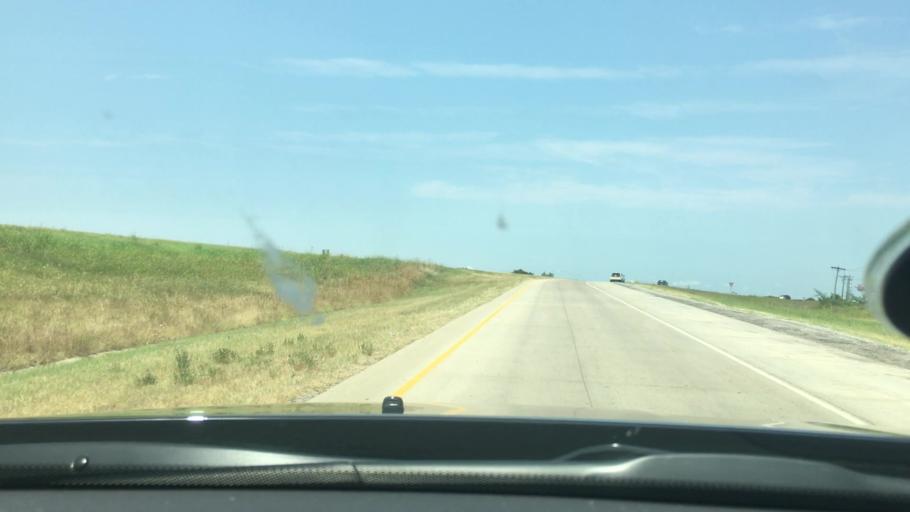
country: US
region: Oklahoma
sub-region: Love County
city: Marietta
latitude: 33.9417
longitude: -97.1342
